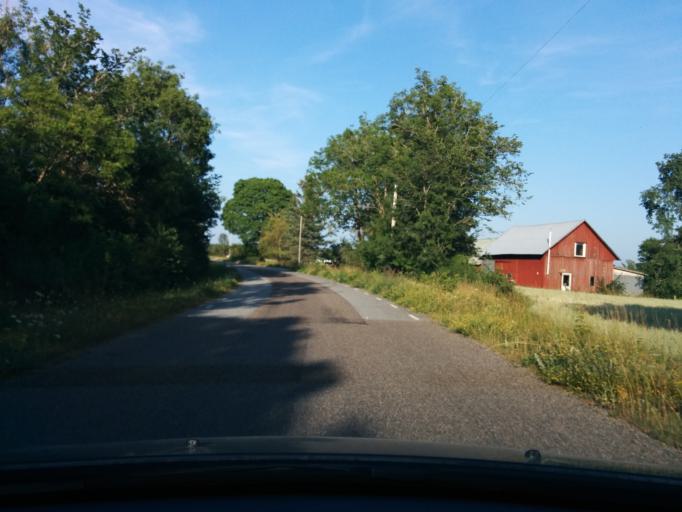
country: SE
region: Gotland
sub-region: Gotland
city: Slite
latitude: 57.5130
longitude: 18.6239
